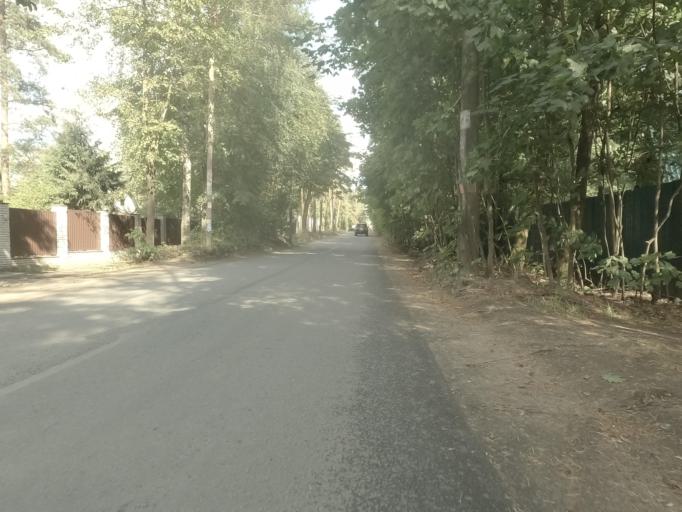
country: RU
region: Leningrad
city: Vsevolozhsk
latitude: 60.0081
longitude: 30.6618
